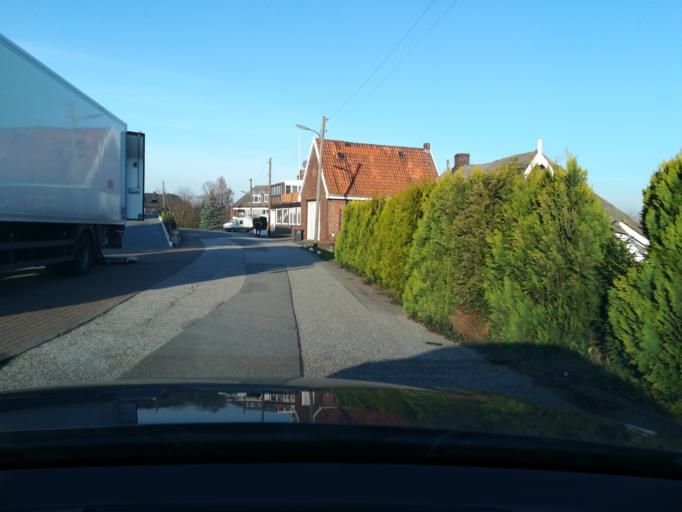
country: DE
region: Hamburg
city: Rothenburgsort
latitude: 53.4780
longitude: 10.0633
